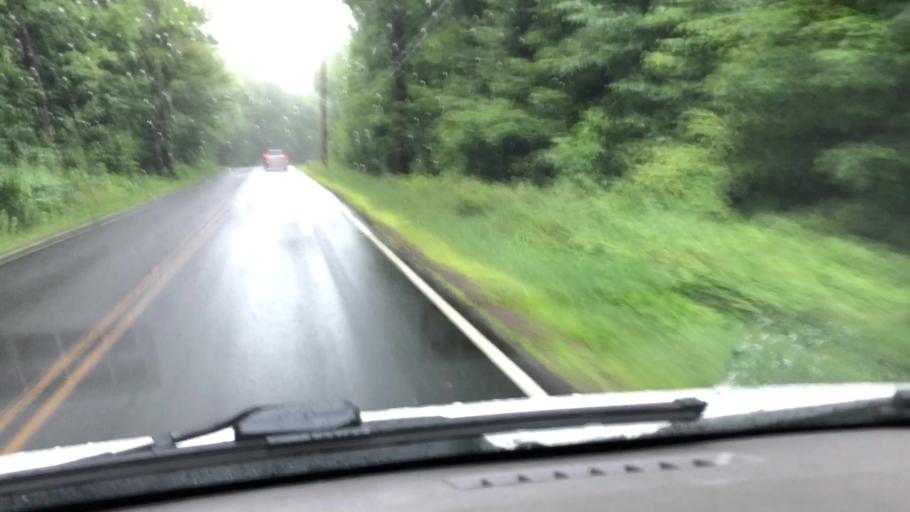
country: US
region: Massachusetts
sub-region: Hampshire County
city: Chesterfield
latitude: 42.4282
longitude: -72.9562
